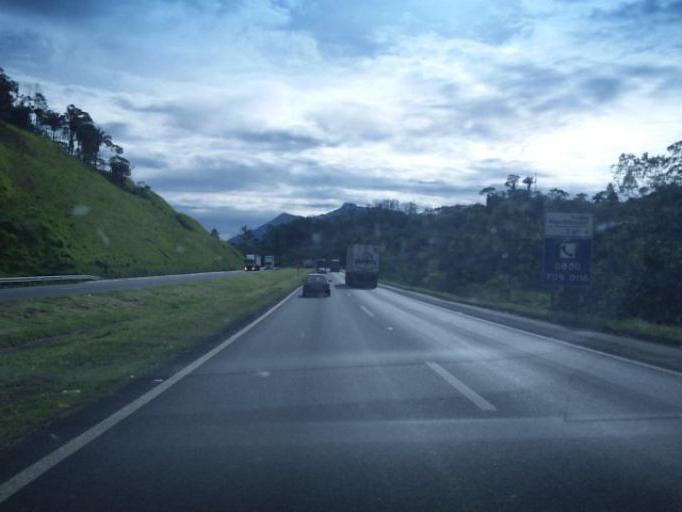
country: BR
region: Parana
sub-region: Antonina
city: Antonina
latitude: -25.1025
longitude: -48.7355
